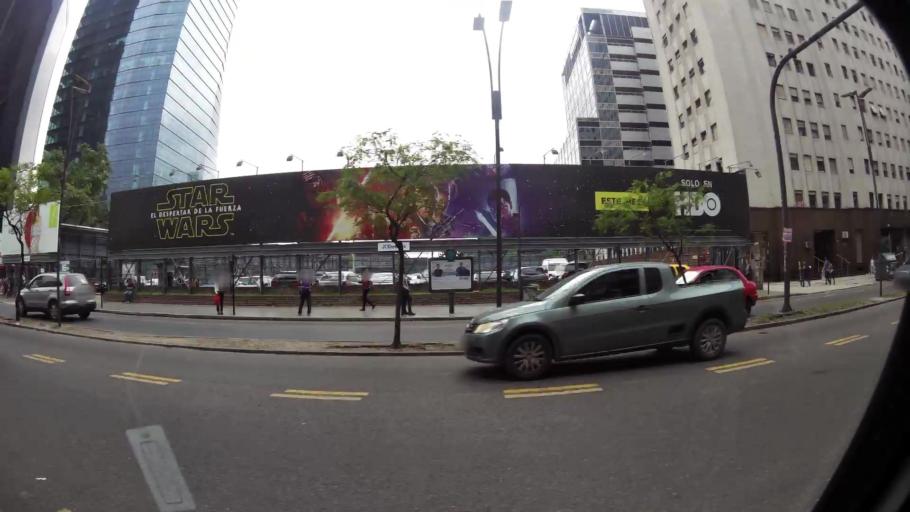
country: AR
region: Buenos Aires F.D.
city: Buenos Aires
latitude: -34.5989
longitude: -58.3710
